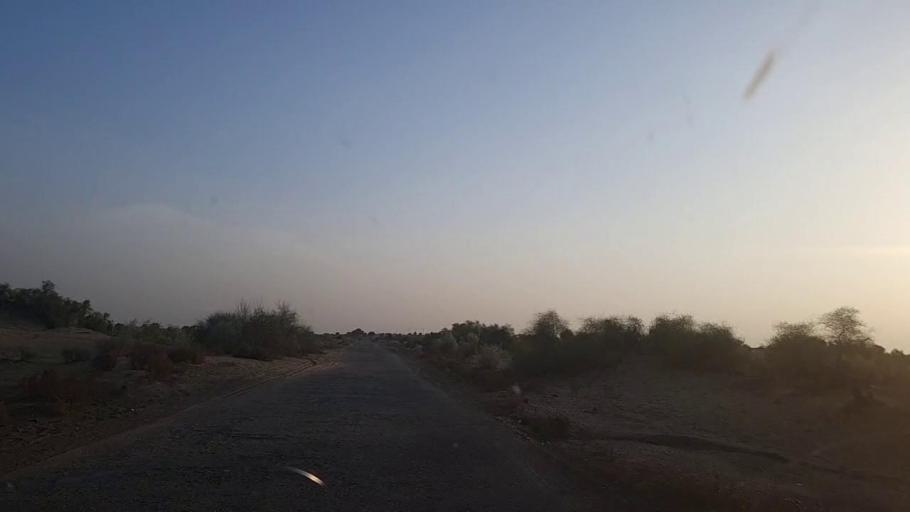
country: PK
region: Sindh
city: Khanpur
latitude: 27.6027
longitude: 69.4323
